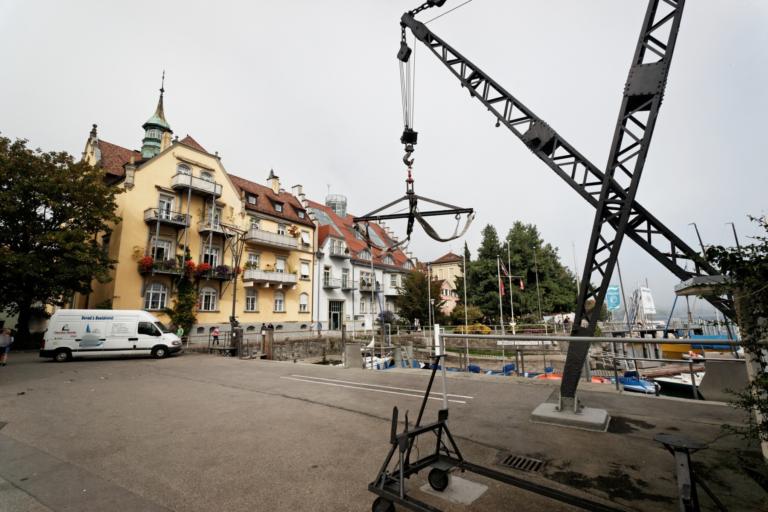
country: DE
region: Bavaria
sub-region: Swabia
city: Lindau
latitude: 47.5446
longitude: 9.6862
